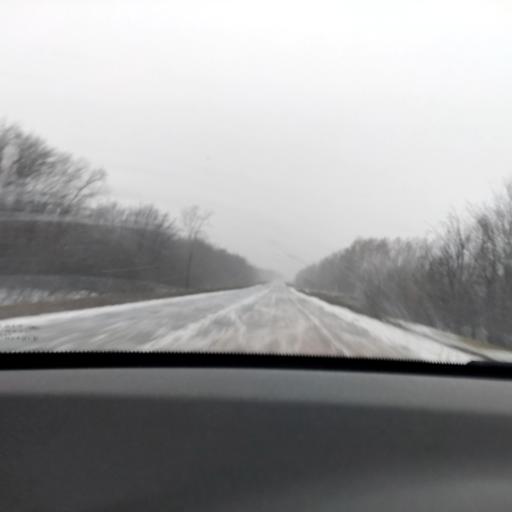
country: RU
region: Samara
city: Novokuybyshevsk
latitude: 52.9497
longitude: 49.8943
